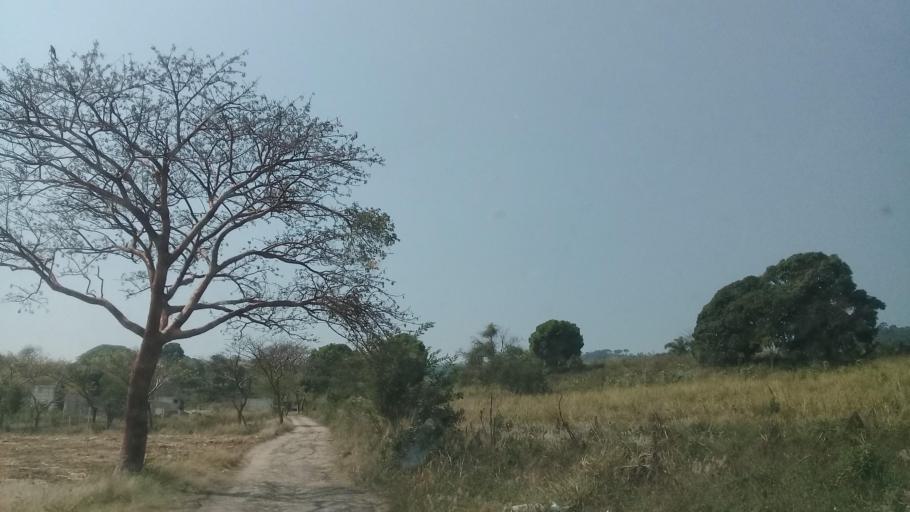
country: MX
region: Veracruz
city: El Castillo
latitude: 19.5680
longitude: -96.8350
